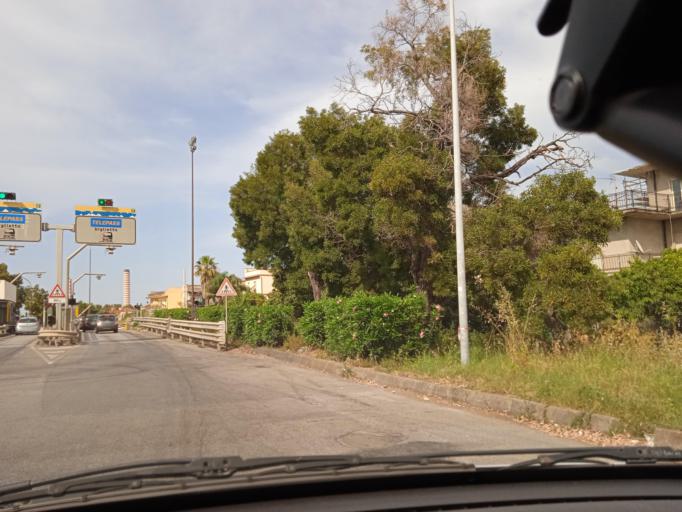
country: IT
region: Sicily
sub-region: Messina
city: San Filippo del Mela
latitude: 38.1891
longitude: 15.2741
